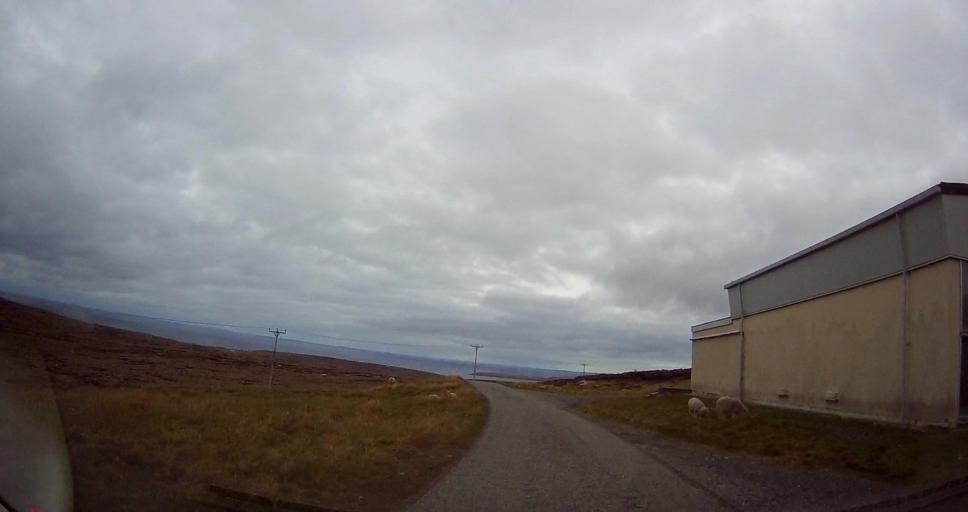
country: GB
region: Scotland
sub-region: Shetland Islands
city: Shetland
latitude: 60.5742
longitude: -1.0677
